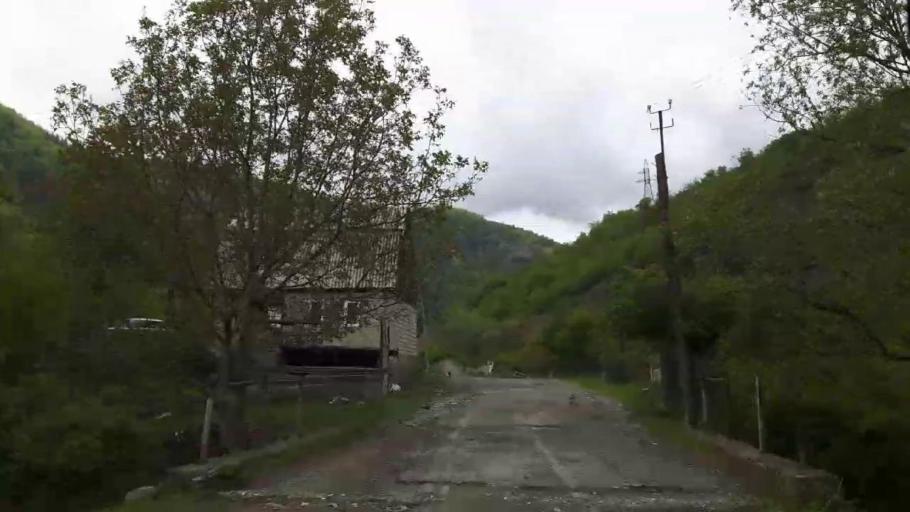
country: GE
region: Shida Kartli
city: Gori
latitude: 41.8684
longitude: 43.9831
